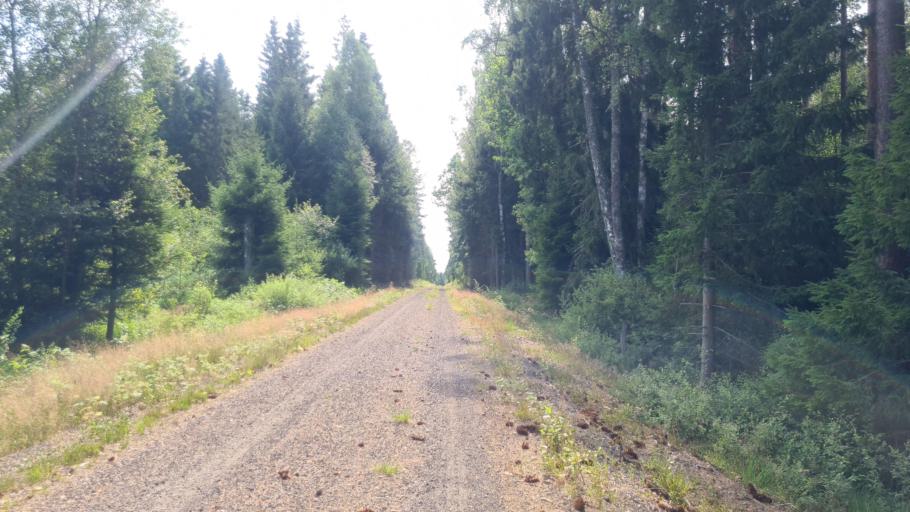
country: SE
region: Kronoberg
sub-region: Ljungby Kommun
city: Lagan
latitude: 56.9475
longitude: 13.9646
